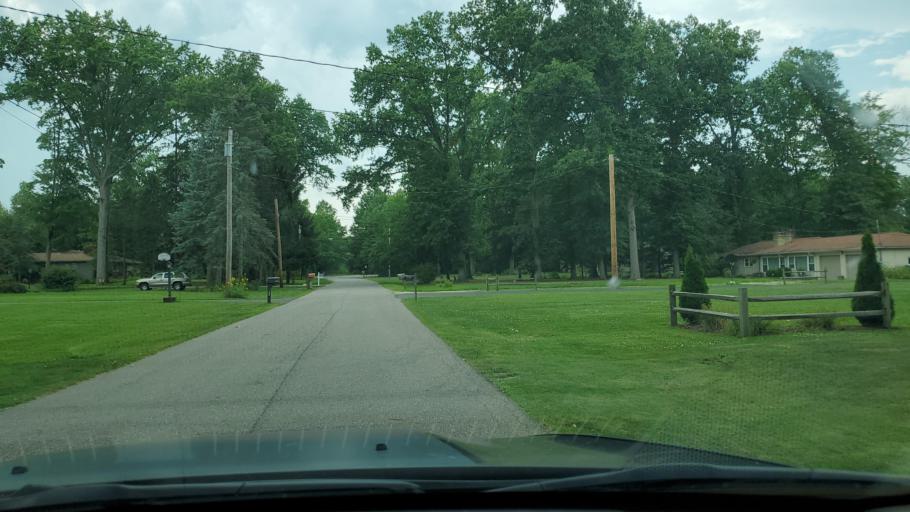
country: US
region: Ohio
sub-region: Trumbull County
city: Bolindale
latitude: 41.2300
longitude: -80.7703
